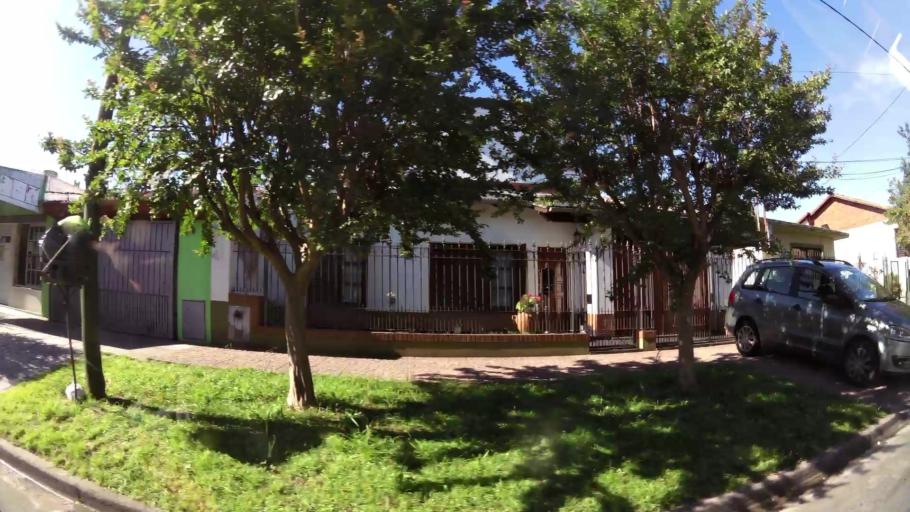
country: AR
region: Buenos Aires
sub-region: Partido de Lomas de Zamora
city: Lomas de Zamora
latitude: -34.7629
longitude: -58.4194
